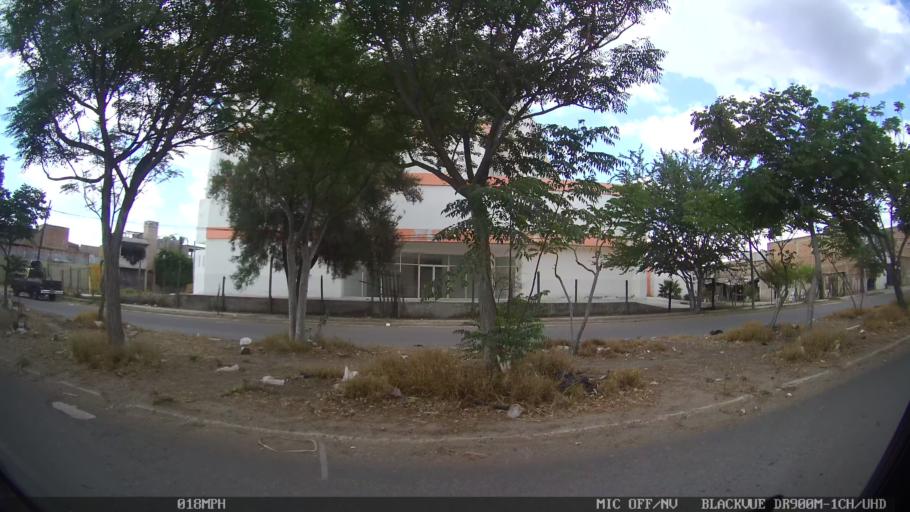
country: MX
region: Jalisco
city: Tlaquepaque
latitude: 20.6710
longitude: -103.2565
